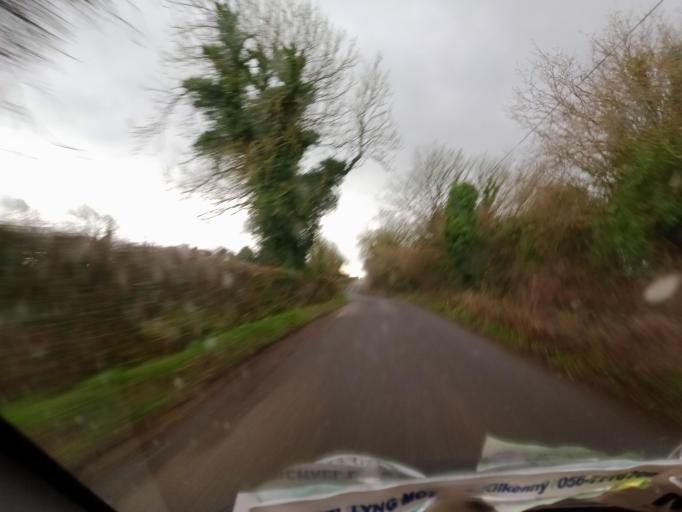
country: IE
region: Munster
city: Fethard
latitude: 52.5464
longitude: -7.7614
